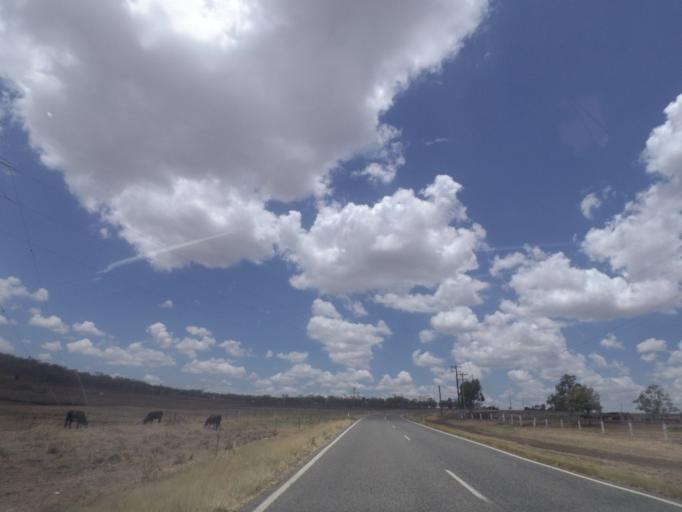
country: AU
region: Queensland
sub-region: Toowoomba
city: Top Camp
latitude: -27.8780
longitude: 151.9681
